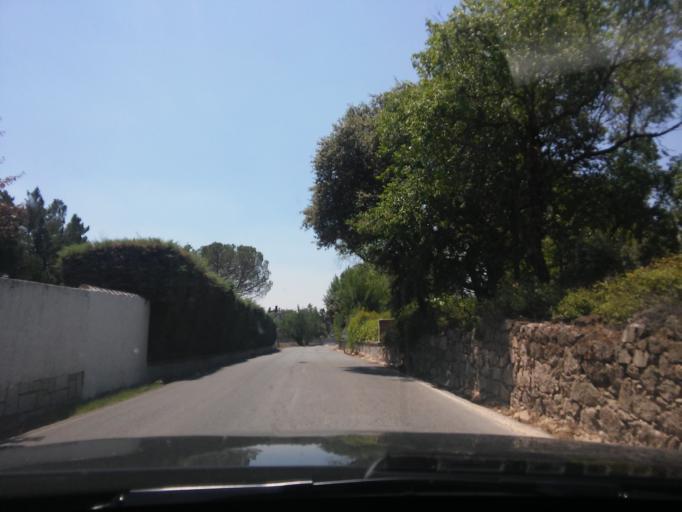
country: ES
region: Madrid
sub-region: Provincia de Madrid
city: Navalquejigo
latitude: 40.6117
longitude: -4.0429
